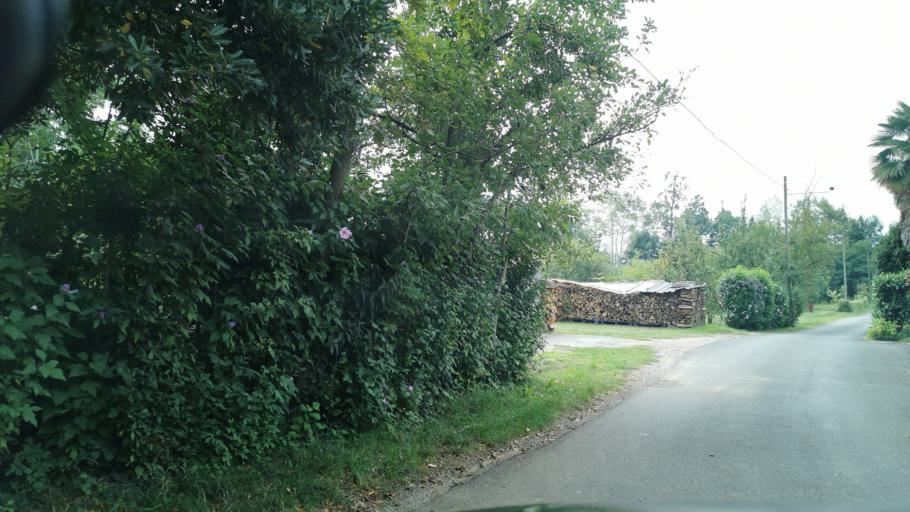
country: IT
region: Piedmont
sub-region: Provincia di Torino
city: Grosso
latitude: 45.2642
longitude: 7.5548
